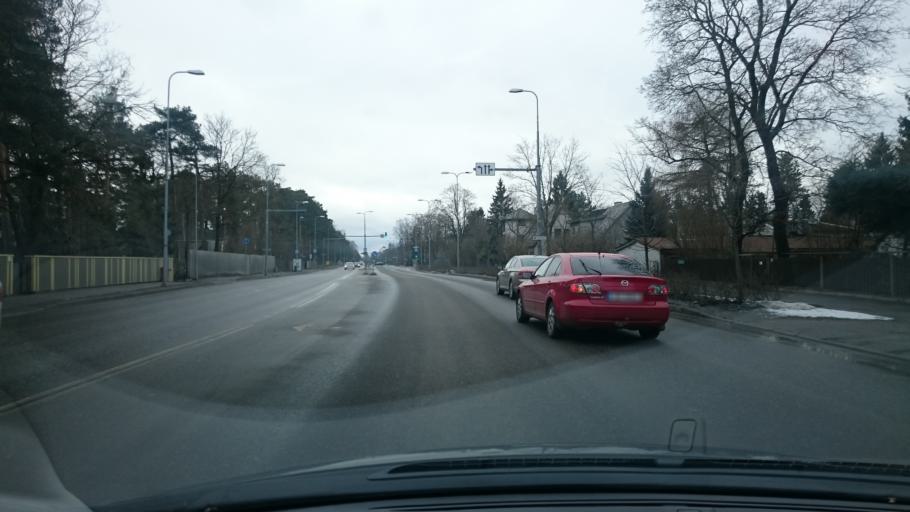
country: EE
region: Harju
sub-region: Tallinna linn
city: Tallinn
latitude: 59.3860
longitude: 24.7175
